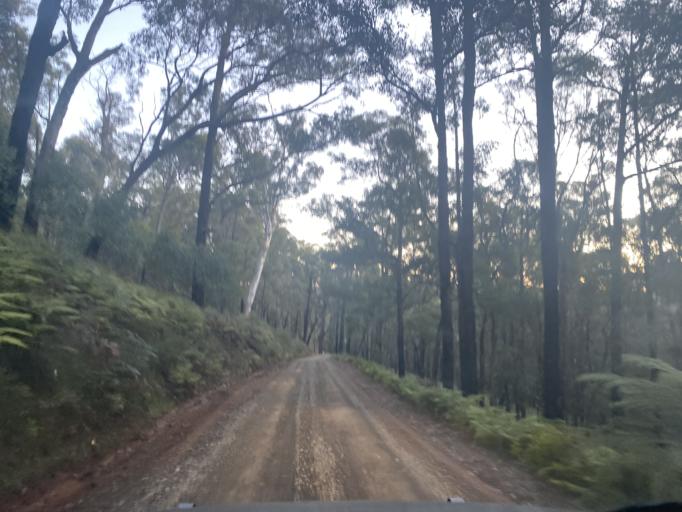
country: AU
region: Victoria
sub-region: Yarra Ranges
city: Healesville
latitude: -37.4302
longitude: 145.5168
